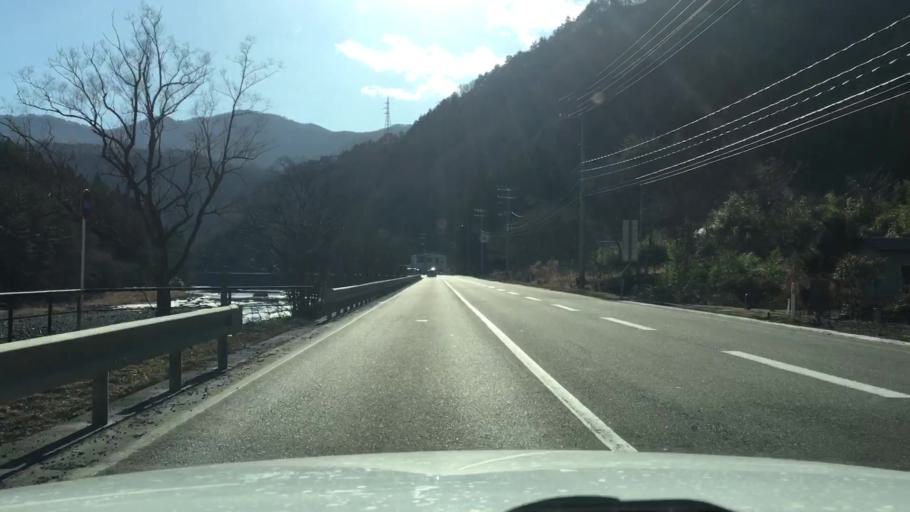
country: JP
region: Iwate
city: Miyako
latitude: 39.6173
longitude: 141.7902
